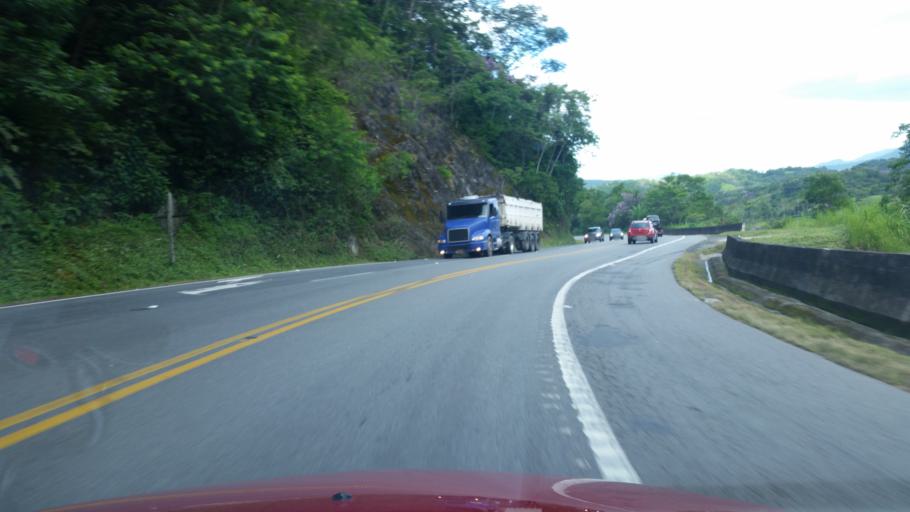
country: BR
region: Sao Paulo
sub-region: Miracatu
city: Miracatu
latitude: -24.2665
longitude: -47.2807
